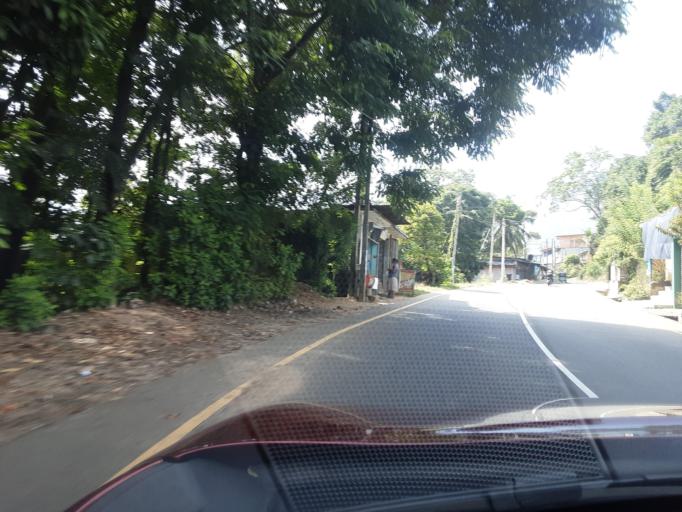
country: LK
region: Uva
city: Badulla
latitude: 6.9786
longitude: 81.0844
